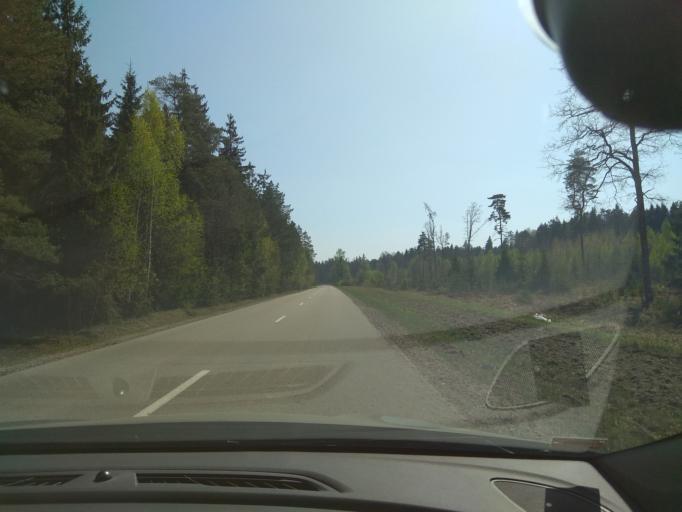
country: LT
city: Linkuva
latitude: 55.9877
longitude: 24.1767
